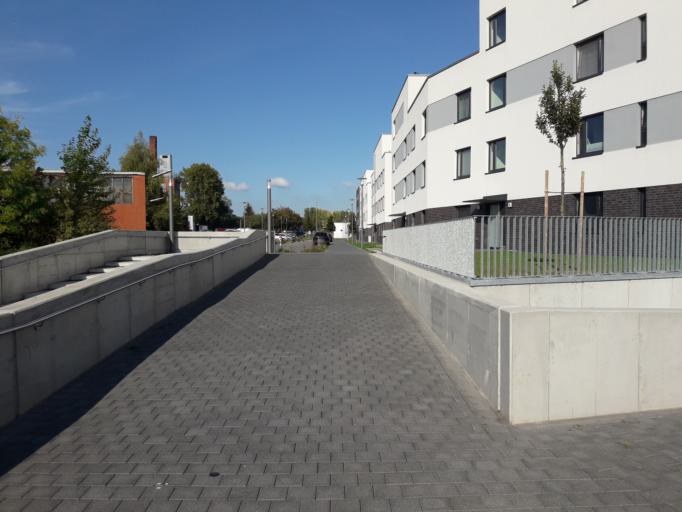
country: DE
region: Schleswig-Holstein
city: Geesthacht
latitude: 53.4301
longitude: 10.3624
